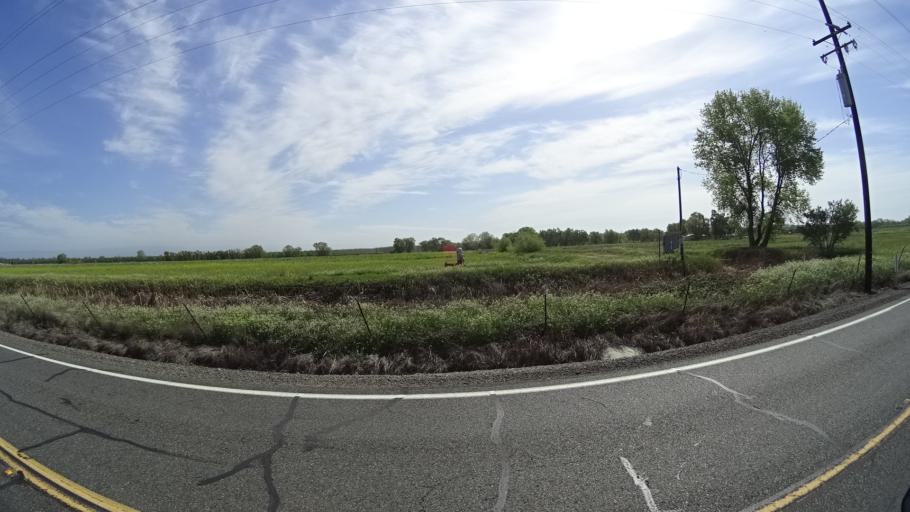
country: US
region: California
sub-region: Glenn County
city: Hamilton City
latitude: 39.6770
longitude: -122.0055
